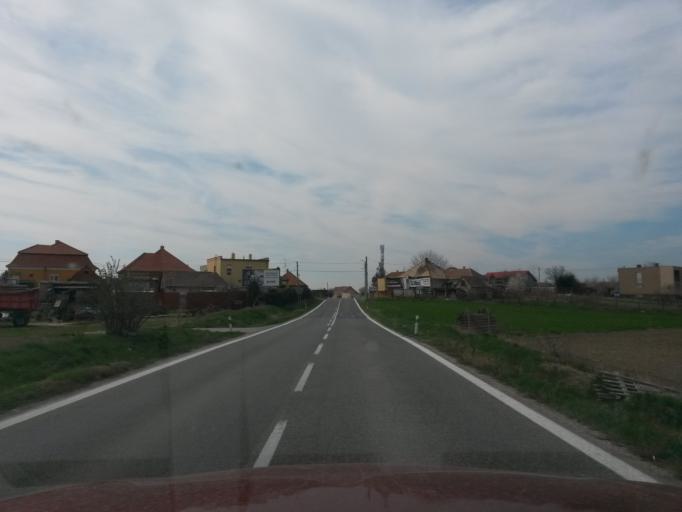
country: SK
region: Nitriansky
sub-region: Okres Nove Zamky
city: Nove Zamky
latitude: 47.9943
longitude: 18.2784
